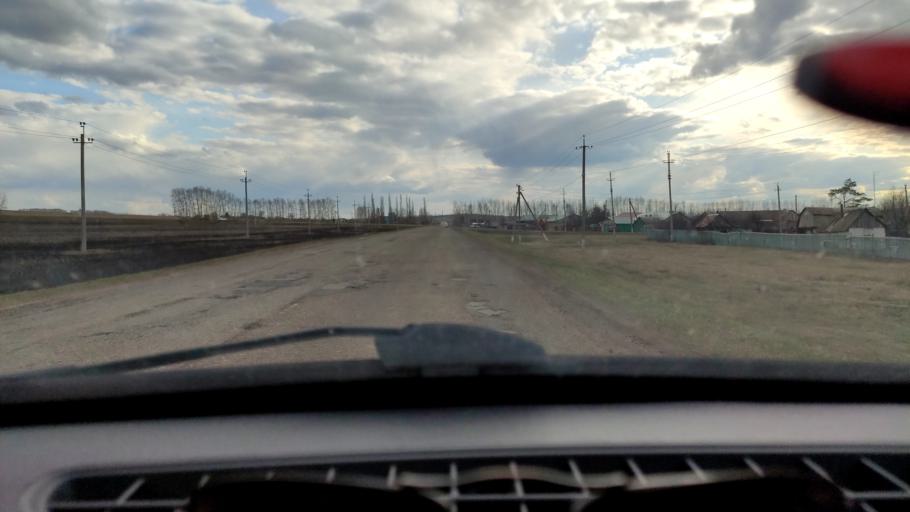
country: RU
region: Bashkortostan
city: Karmaskaly
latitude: 54.3929
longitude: 56.2413
